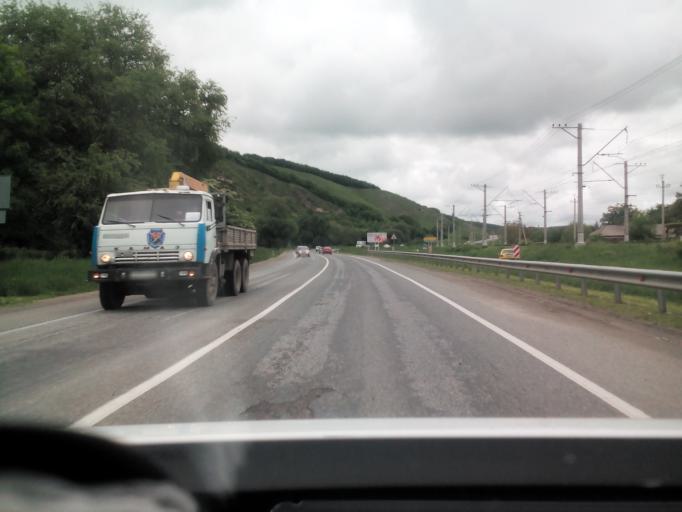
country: RU
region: Stavropol'skiy
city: Yasnaya Polyana
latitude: 43.9905
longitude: 42.7942
